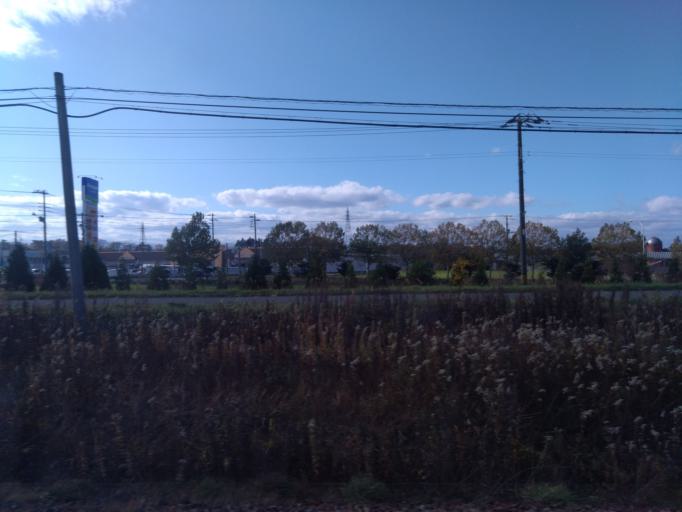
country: JP
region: Hokkaido
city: Kitahiroshima
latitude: 42.9072
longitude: 141.5742
